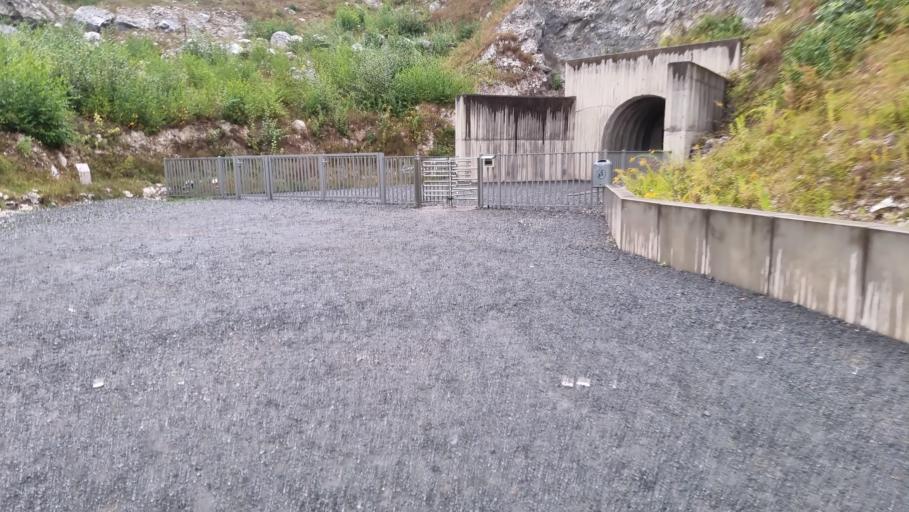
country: DE
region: Thuringia
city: Niedersachswerfen
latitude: 51.5346
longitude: 10.7572
